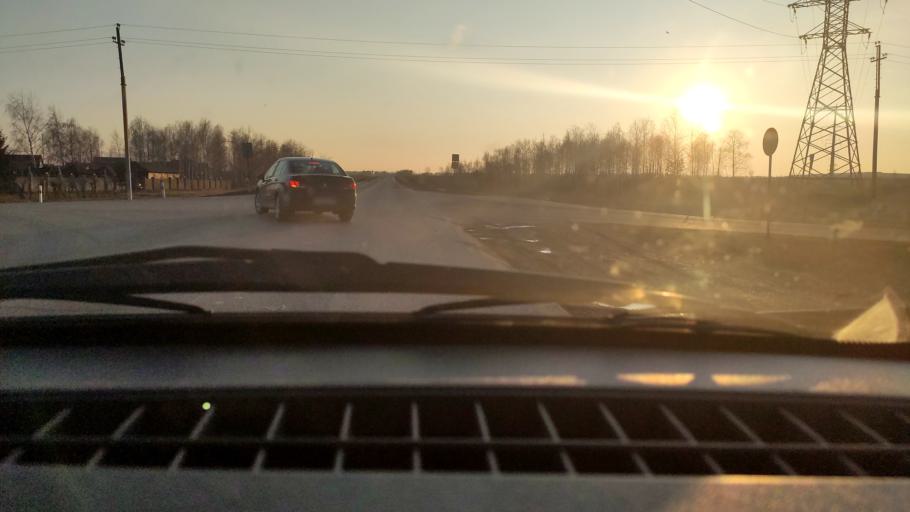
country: RU
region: Bashkortostan
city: Davlekanovo
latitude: 54.2383
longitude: 55.0474
